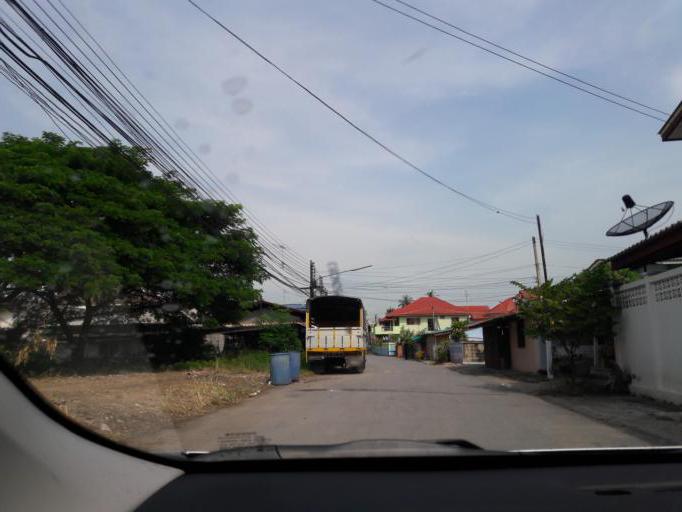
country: TH
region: Ang Thong
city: Ang Thong
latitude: 14.5824
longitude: 100.4632
